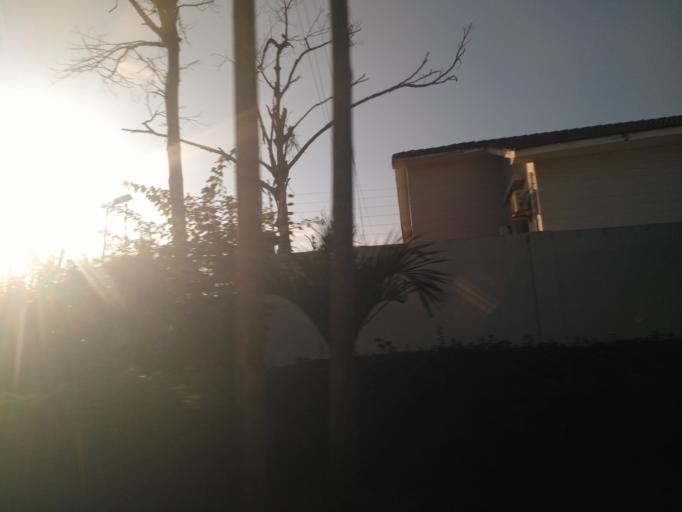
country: TZ
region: Dar es Salaam
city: Magomeni
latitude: -6.7631
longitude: 39.2802
